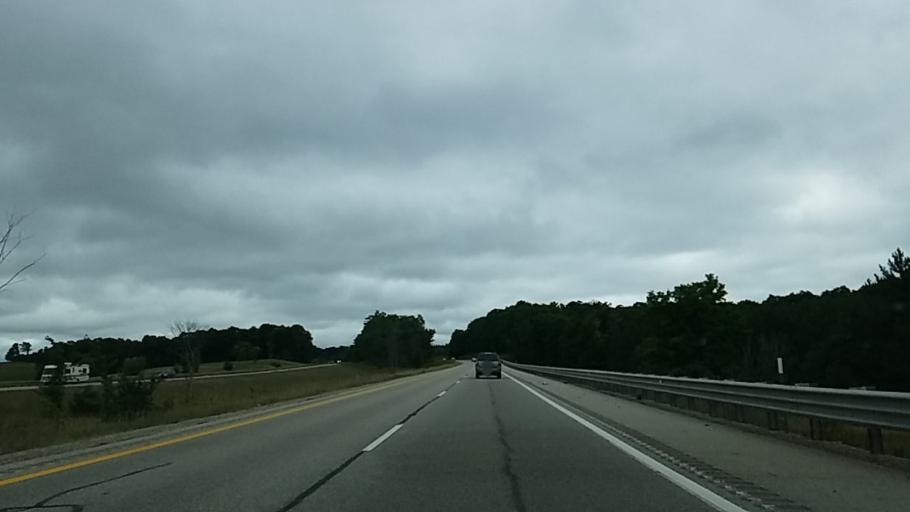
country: US
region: Michigan
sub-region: Otsego County
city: Gaylord
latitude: 45.0858
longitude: -84.6900
